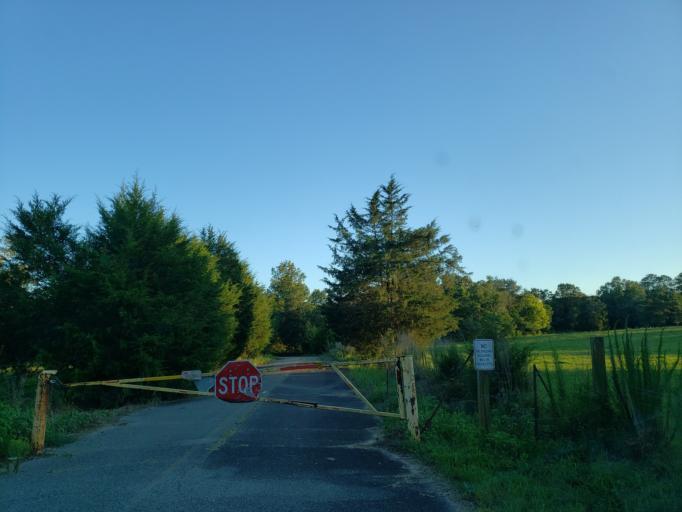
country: US
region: Georgia
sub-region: Bartow County
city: Euharlee
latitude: 34.0778
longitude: -84.9120
